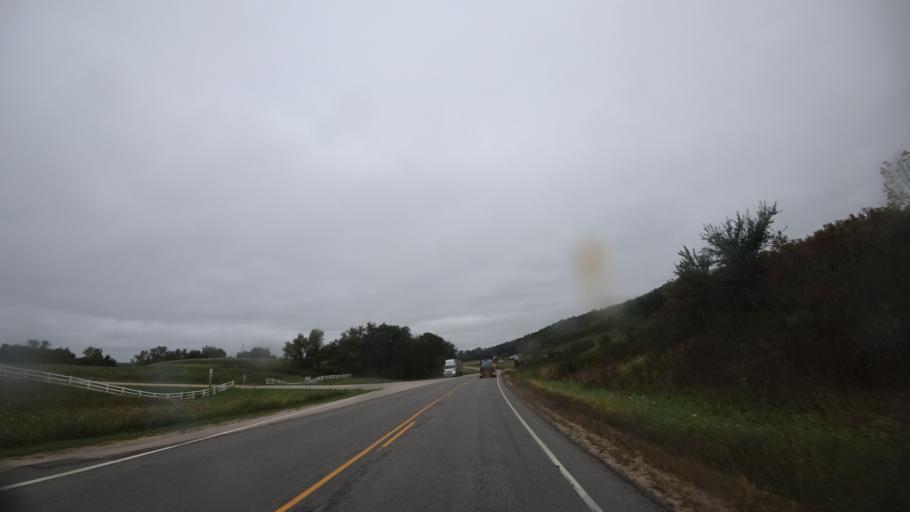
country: US
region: Wisconsin
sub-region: Crawford County
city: Prairie du Chien
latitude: 43.0270
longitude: -91.0199
